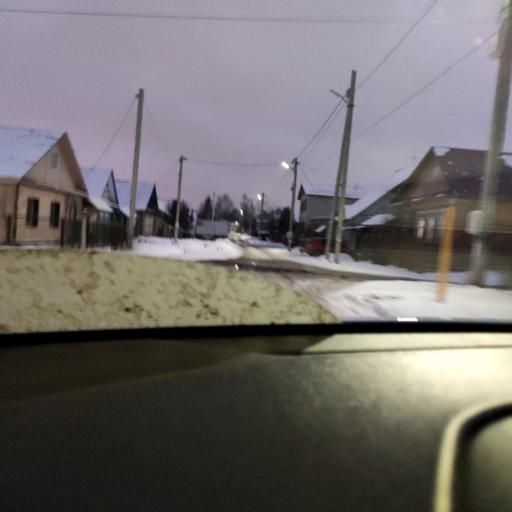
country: RU
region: Tatarstan
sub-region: Gorod Kazan'
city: Kazan
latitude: 55.8797
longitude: 49.0767
